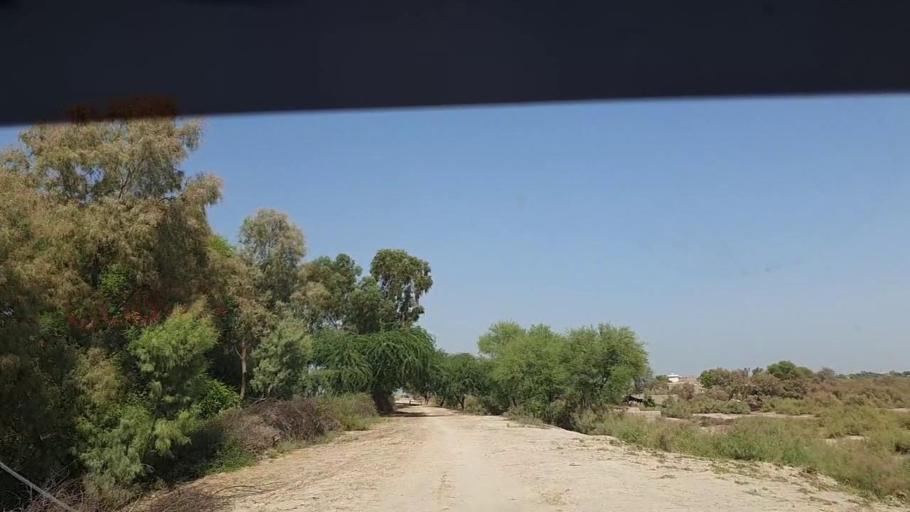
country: PK
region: Sindh
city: Kandhkot
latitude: 28.1790
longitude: 69.1515
